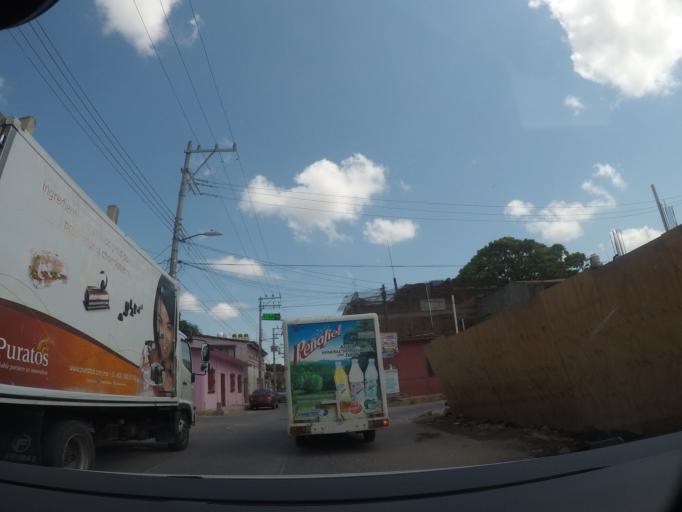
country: MX
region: Oaxaca
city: Juchitan de Zaragoza
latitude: 16.4361
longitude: -95.0211
